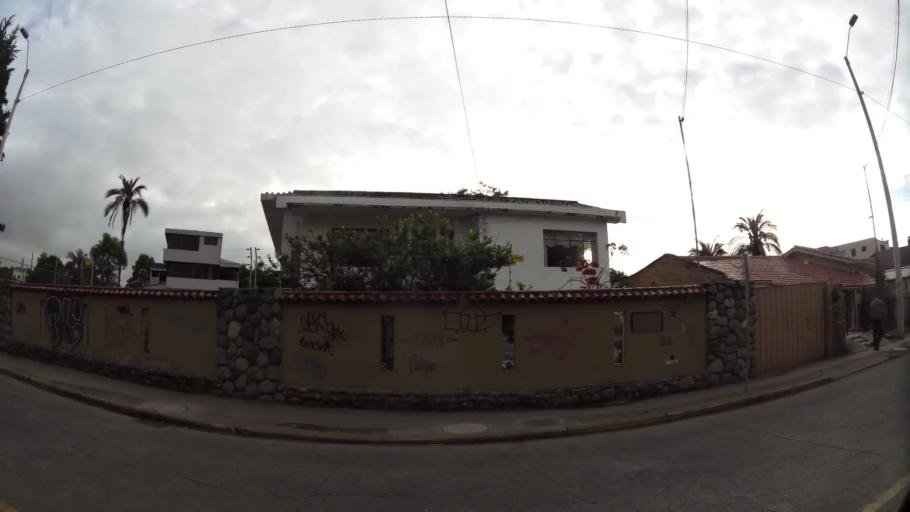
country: EC
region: Azuay
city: Cuenca
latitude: -2.9073
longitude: -79.0003
